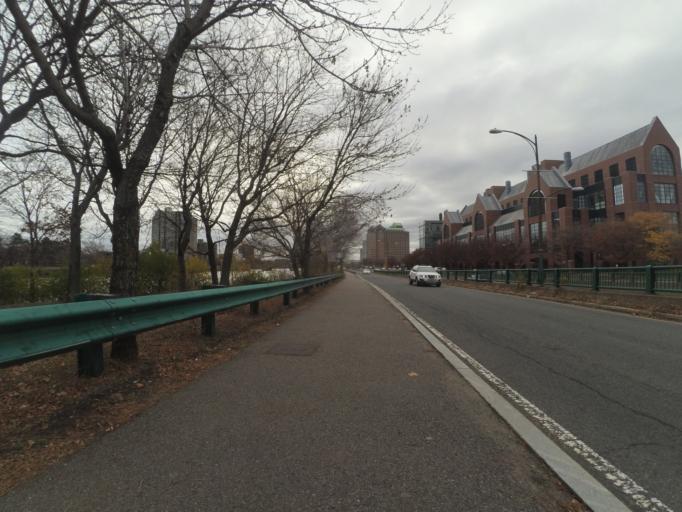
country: US
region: Massachusetts
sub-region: Middlesex County
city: Cambridge
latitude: 42.3639
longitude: -71.1178
